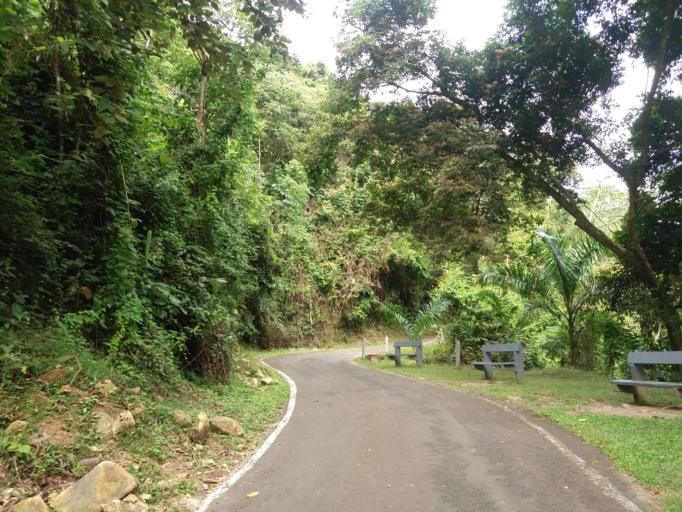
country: PA
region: Panama
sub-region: Distrito de Panama
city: Ancon
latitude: 8.9556
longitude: -79.5486
